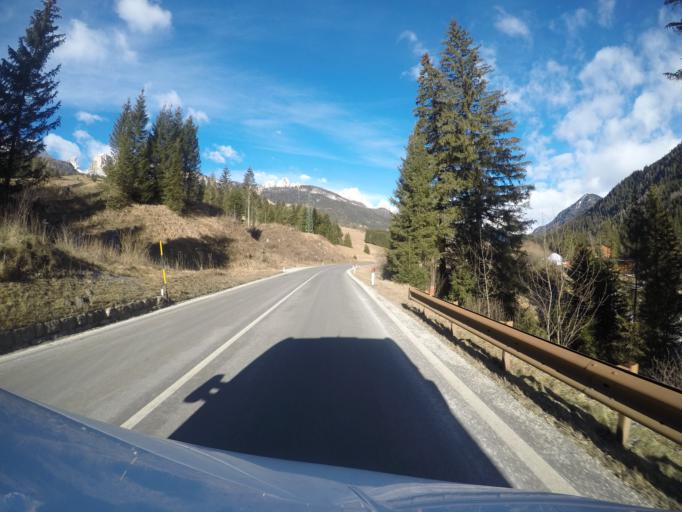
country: IT
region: Trentino-Alto Adige
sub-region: Provincia di Trento
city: Vigo di Fassa
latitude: 46.4084
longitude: 11.6767
